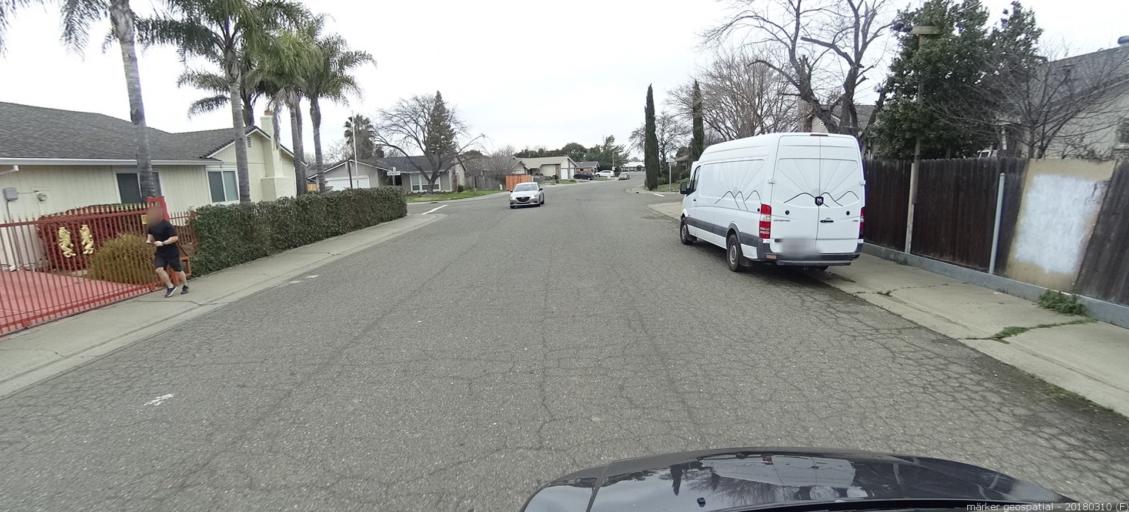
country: US
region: California
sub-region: Sacramento County
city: Florin
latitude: 38.4945
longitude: -121.3828
